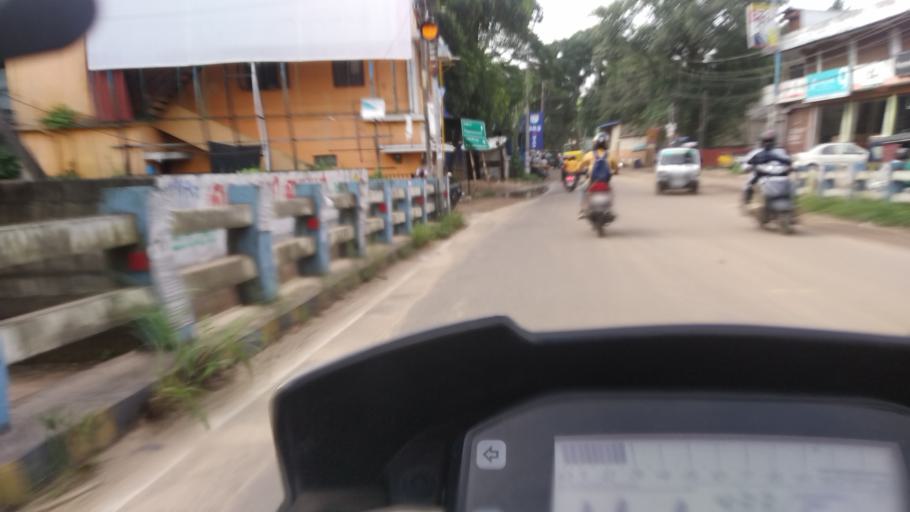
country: IN
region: Kerala
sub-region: Ernakulam
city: Cochin
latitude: 9.9782
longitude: 76.3142
